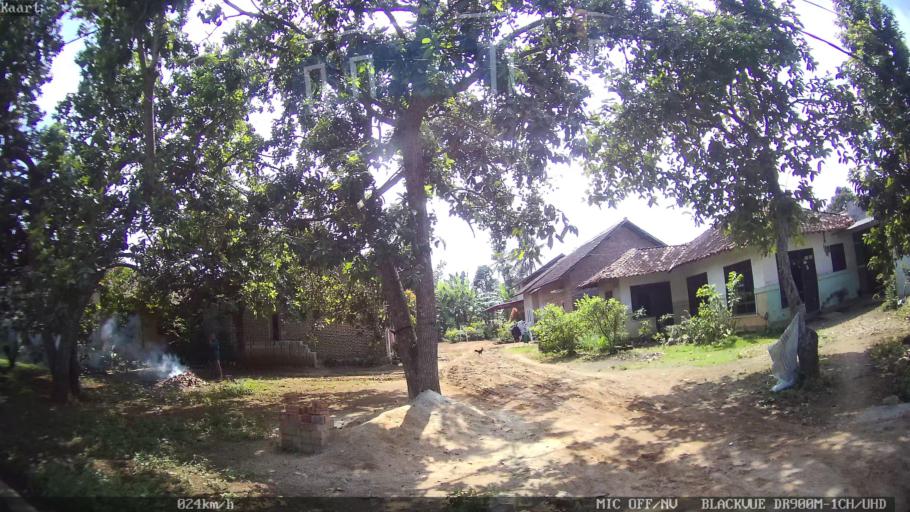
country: ID
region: Lampung
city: Kedaton
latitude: -5.3488
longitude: 105.2893
